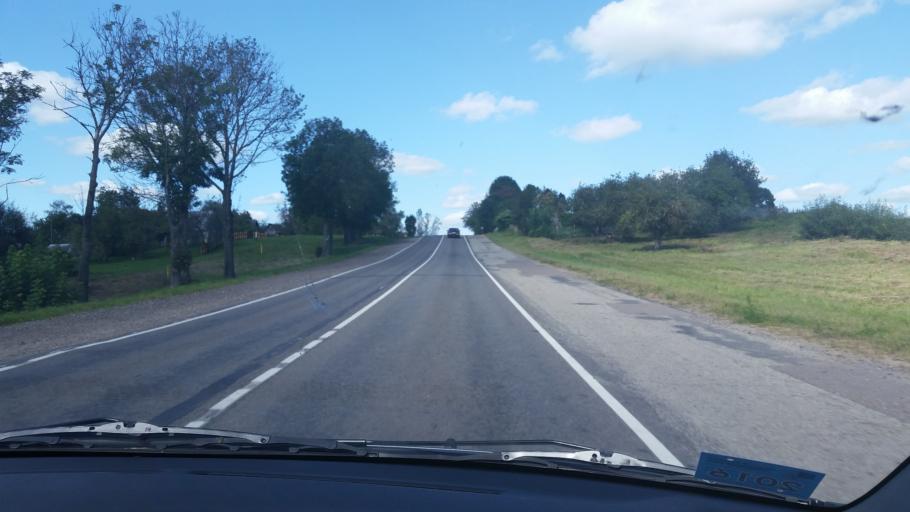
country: BY
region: Vitebsk
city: Vitebsk
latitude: 55.1096
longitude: 30.2832
